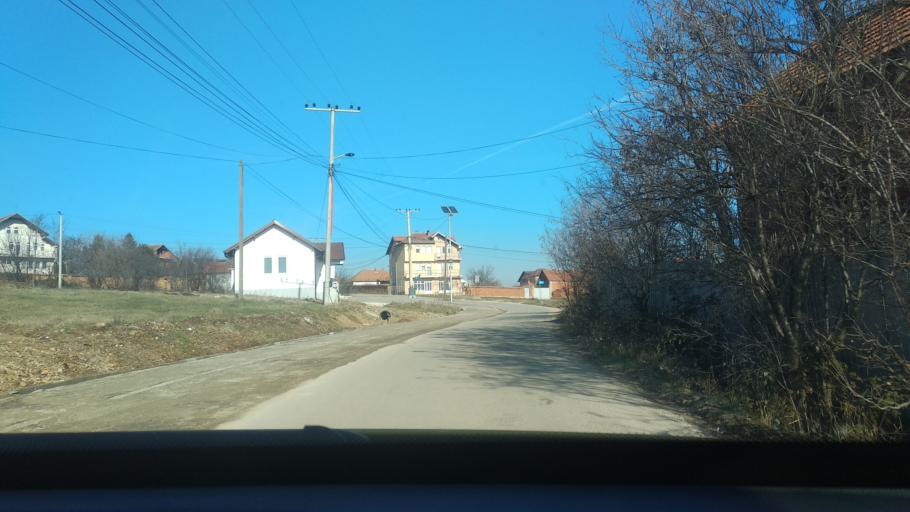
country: XK
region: Pristina
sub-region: Komuna e Gracanices
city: Glanica
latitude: 42.6045
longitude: 21.0281
